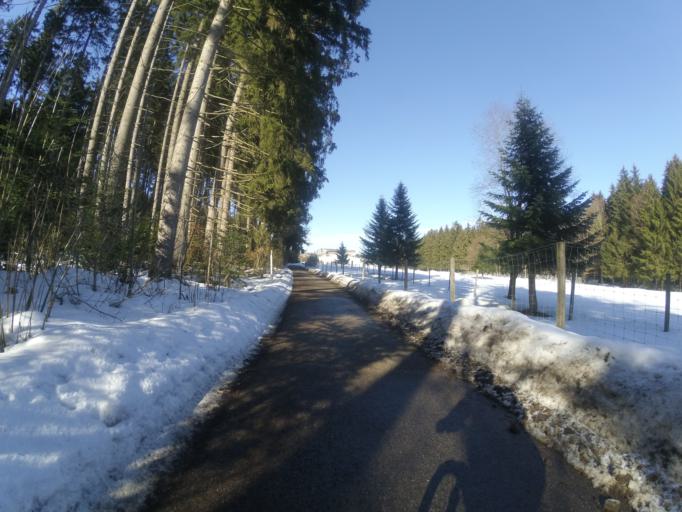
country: DE
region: Bavaria
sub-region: Upper Bavaria
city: Feldkirchen-Westerham
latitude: 47.9246
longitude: 11.8140
